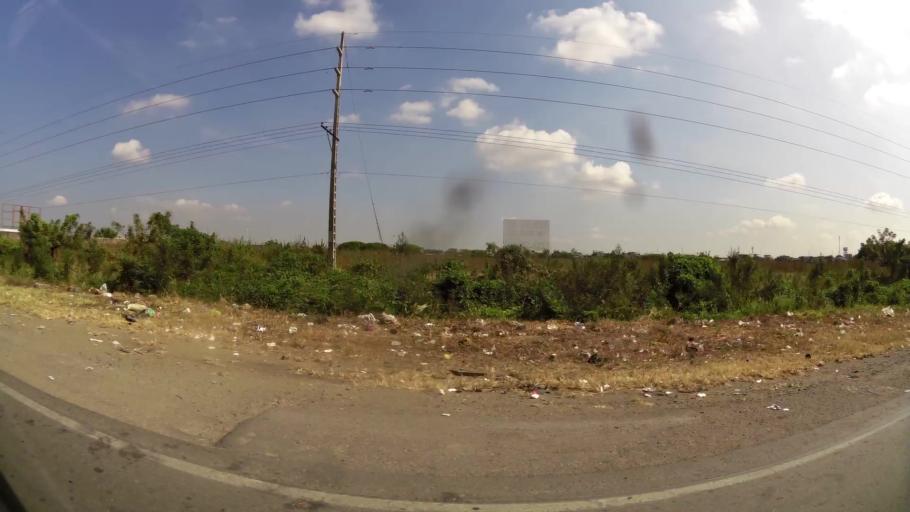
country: EC
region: Guayas
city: Eloy Alfaro
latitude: -2.1815
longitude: -79.8070
